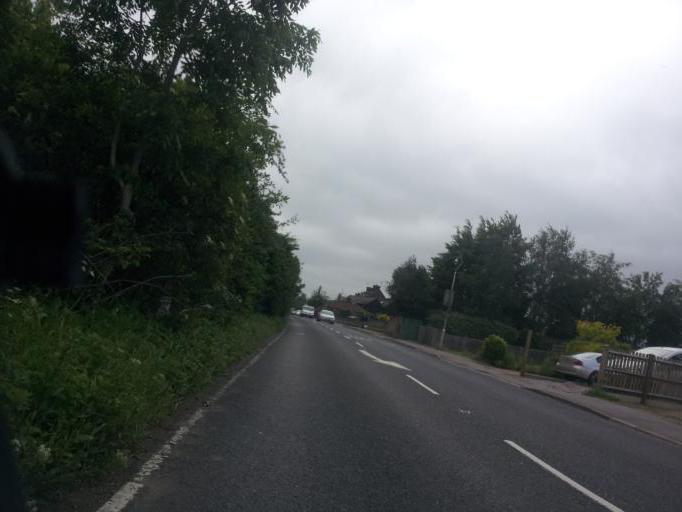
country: GB
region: England
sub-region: Kent
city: Wateringbury
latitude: 51.2491
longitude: 0.4197
